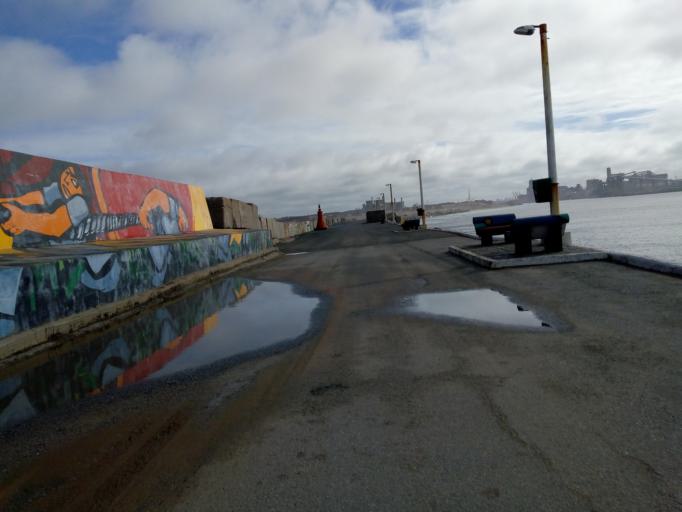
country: AR
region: Buenos Aires
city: Necochea
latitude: -38.5849
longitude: -58.6947
